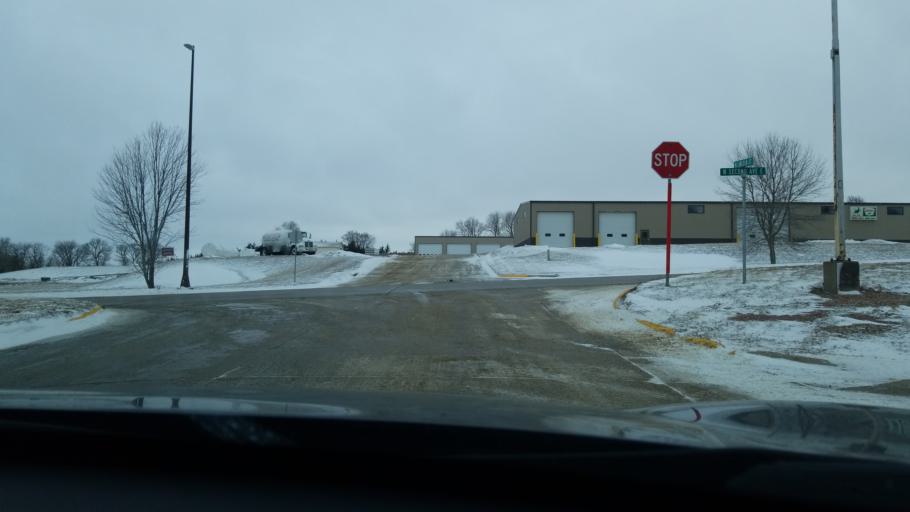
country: US
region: Iowa
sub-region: Lyon County
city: Rock Rapids
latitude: 43.4328
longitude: -96.1581
